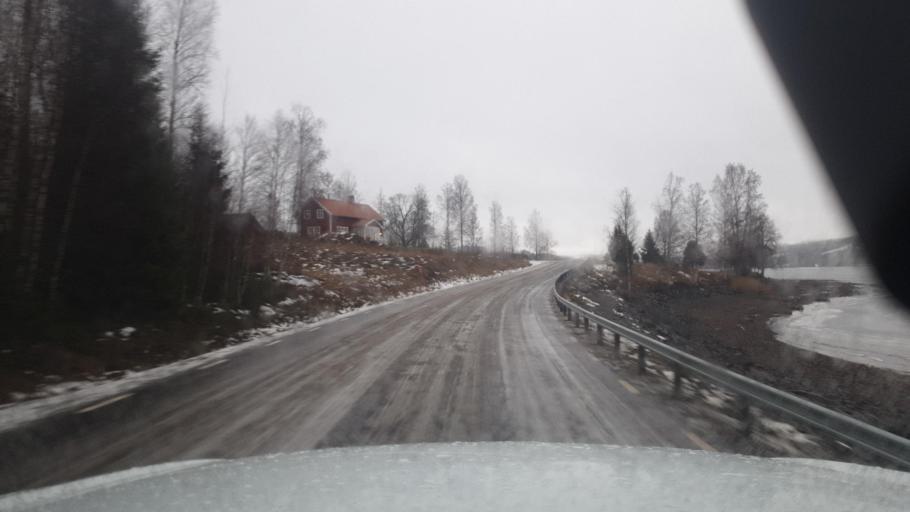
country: SE
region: Vaermland
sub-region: Torsby Kommun
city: Torsby
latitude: 59.9838
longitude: 12.7886
